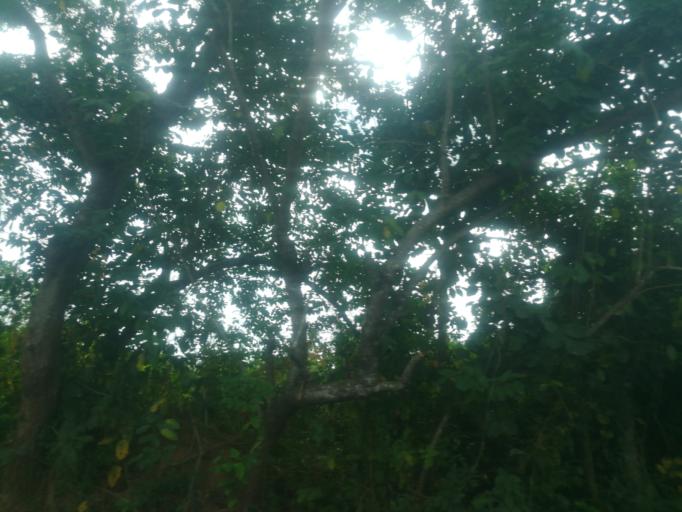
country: NG
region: Ogun
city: Ayetoro
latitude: 7.3025
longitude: 3.0752
